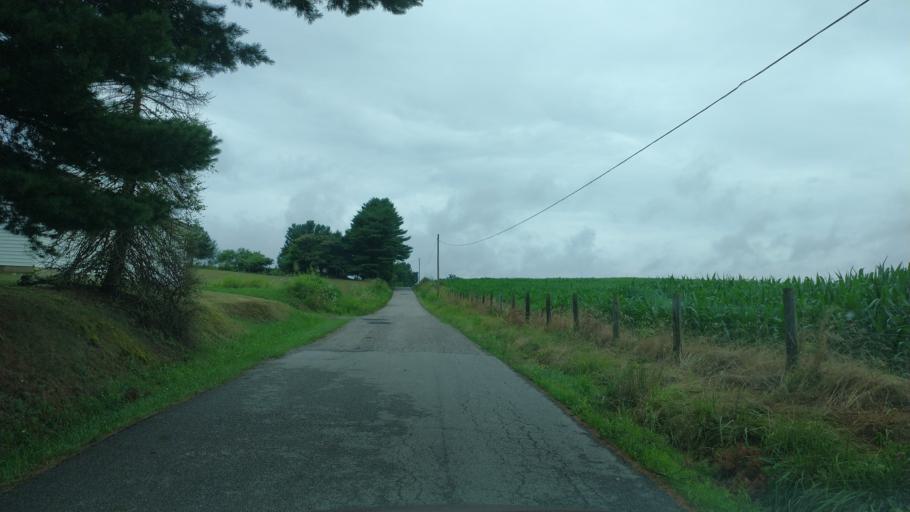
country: US
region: West Virginia
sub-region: Mason County
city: New Haven
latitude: 38.9262
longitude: -81.9603
